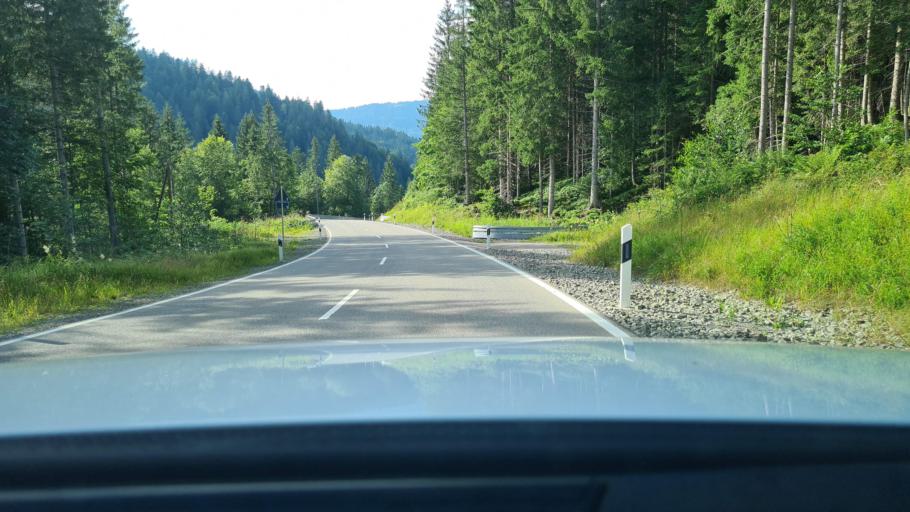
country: DE
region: Bavaria
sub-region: Swabia
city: Balderschwang
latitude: 47.4400
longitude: 10.1413
